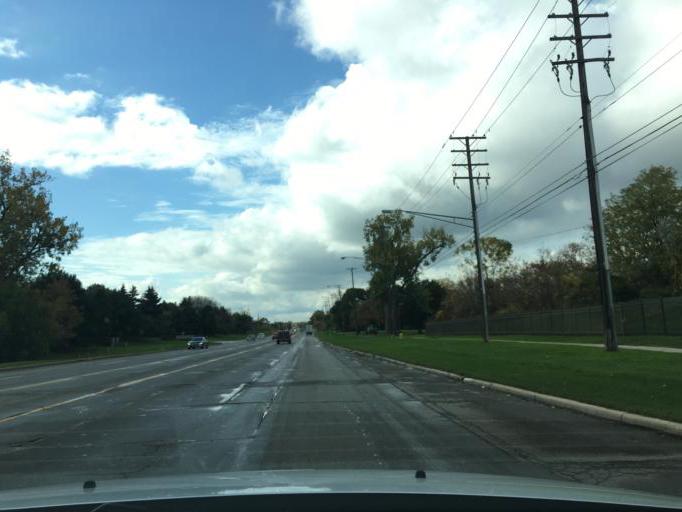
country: US
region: Michigan
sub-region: Wayne County
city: Dearborn
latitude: 42.3030
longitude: -83.1947
